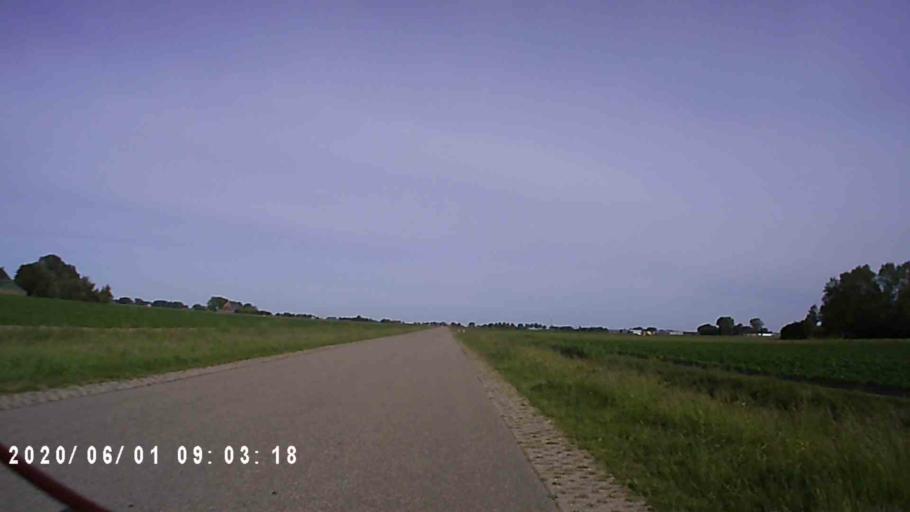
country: NL
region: Friesland
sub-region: Gemeente Ferwerderadiel
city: Hallum
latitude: 53.2938
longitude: 5.7849
